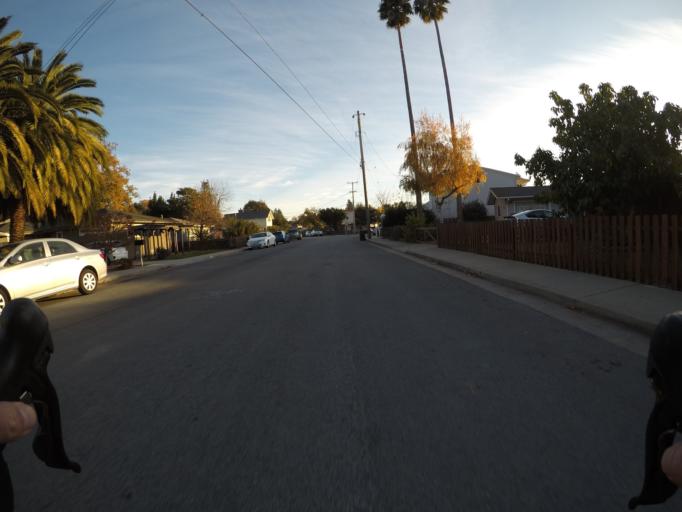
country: US
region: California
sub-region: Santa Cruz County
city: Pasatiempo
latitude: 36.9882
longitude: -122.0165
